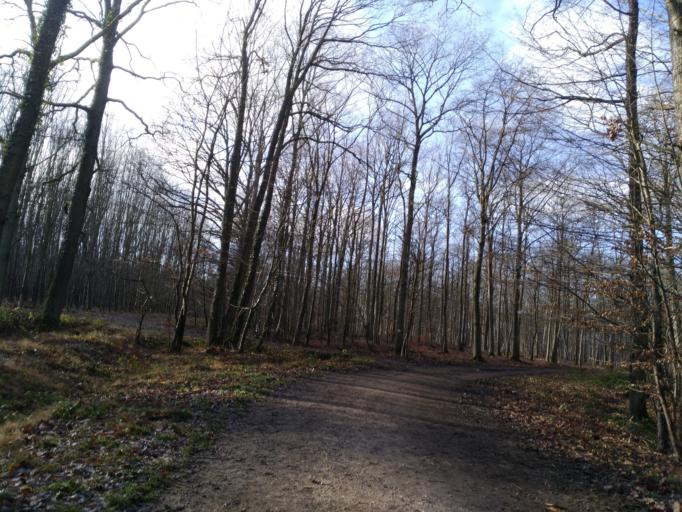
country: FR
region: Ile-de-France
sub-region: Departement des Yvelines
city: Elancourt
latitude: 48.8025
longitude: 1.9376
